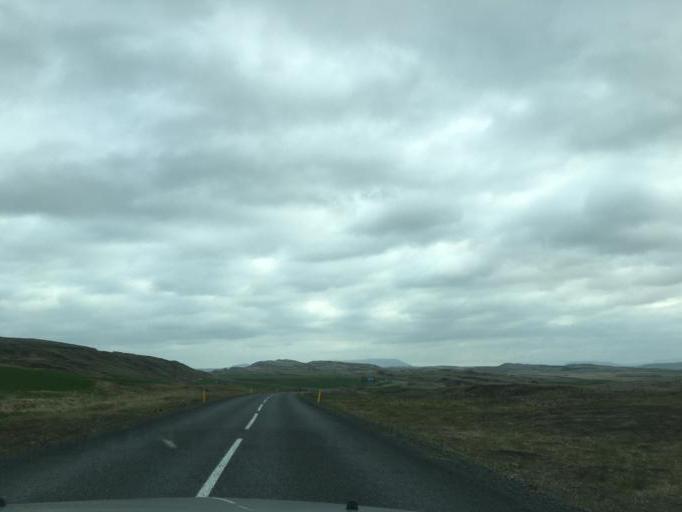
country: IS
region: South
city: Vestmannaeyjar
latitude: 64.2278
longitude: -20.2493
